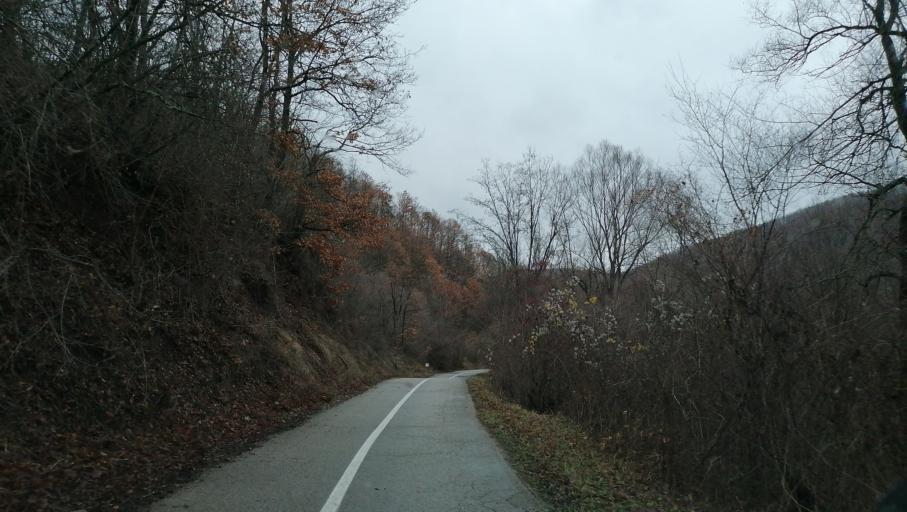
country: RS
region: Central Serbia
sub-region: Pirotski Okrug
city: Dimitrovgrad
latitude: 42.9641
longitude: 22.7825
